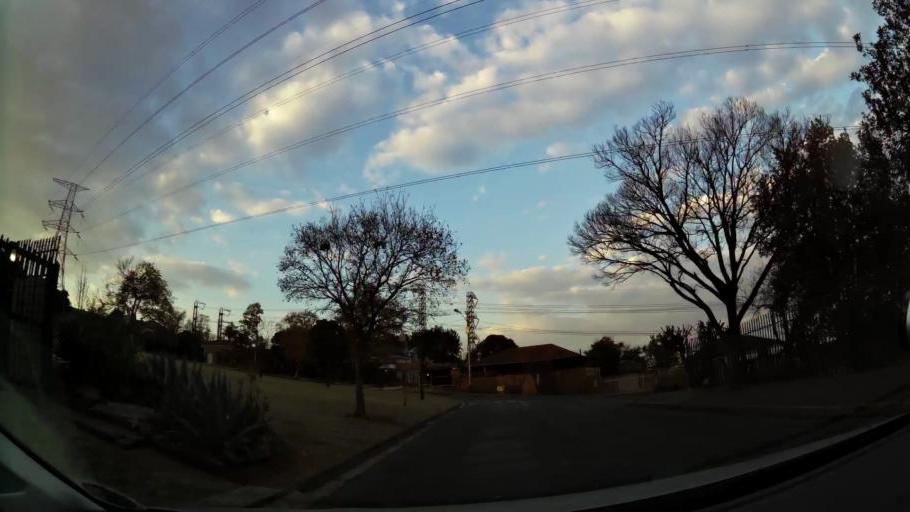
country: ZA
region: Gauteng
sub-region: Ekurhuleni Metropolitan Municipality
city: Germiston
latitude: -26.1912
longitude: 28.1450
